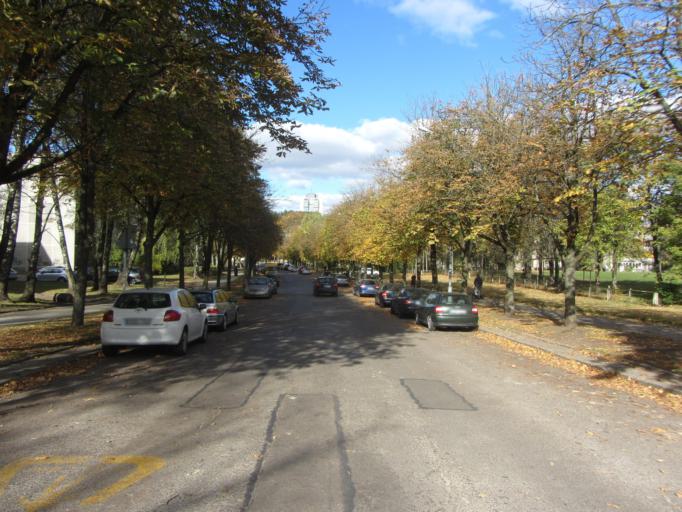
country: LT
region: Vilnius County
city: Lazdynai
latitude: 54.6751
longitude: 25.2099
